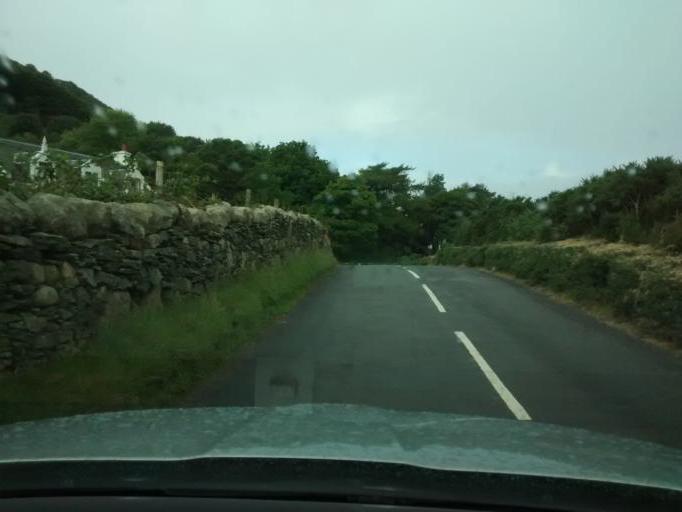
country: GB
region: Scotland
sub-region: North Ayrshire
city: Isle of Arran
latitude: 55.7019
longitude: -5.2855
